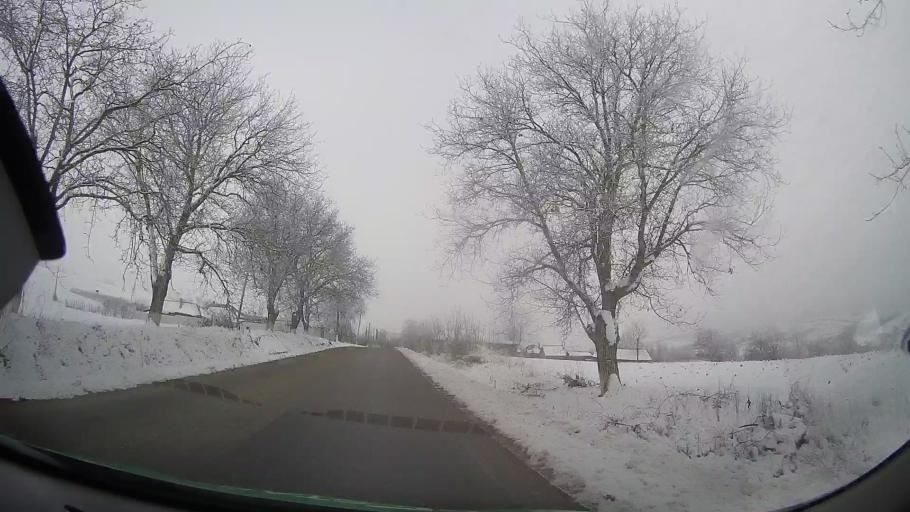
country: RO
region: Bacau
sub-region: Comuna Oncesti
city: Oncesti
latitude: 46.4453
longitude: 27.2649
